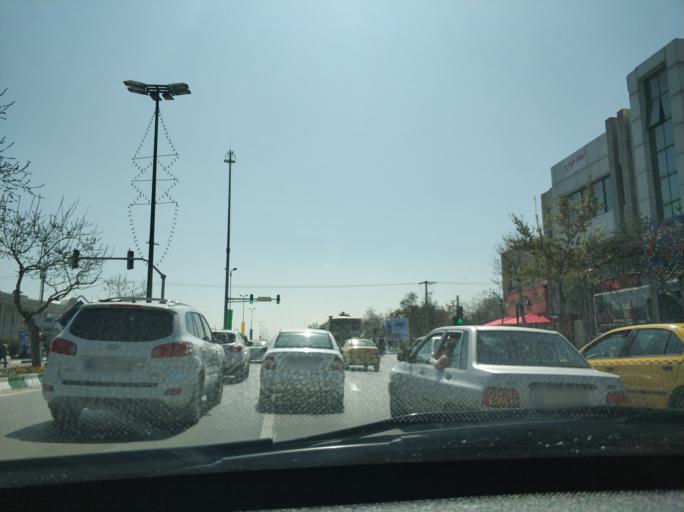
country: IR
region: Razavi Khorasan
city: Mashhad
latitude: 36.2582
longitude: 59.6085
